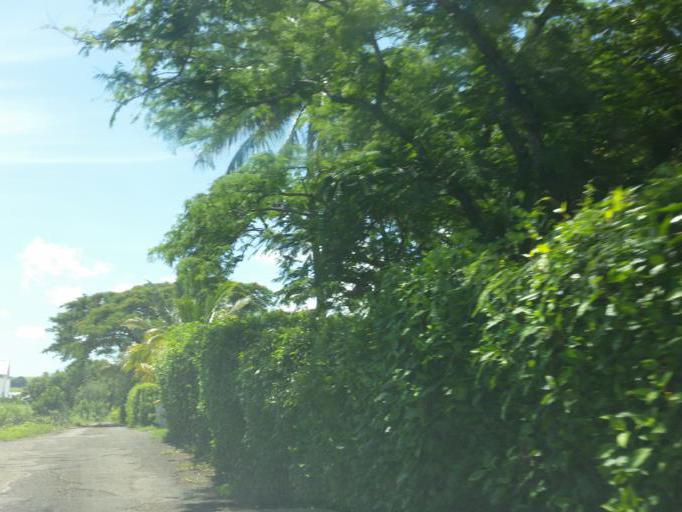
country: RE
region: Reunion
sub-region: Reunion
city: Sainte-Marie
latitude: -20.9061
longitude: 55.5178
